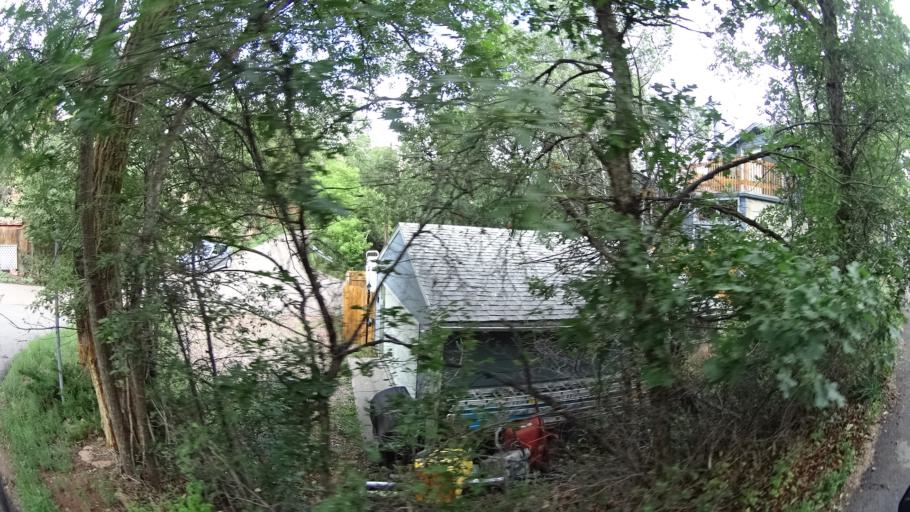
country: US
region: Colorado
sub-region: El Paso County
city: Manitou Springs
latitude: 38.8549
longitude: -104.9111
